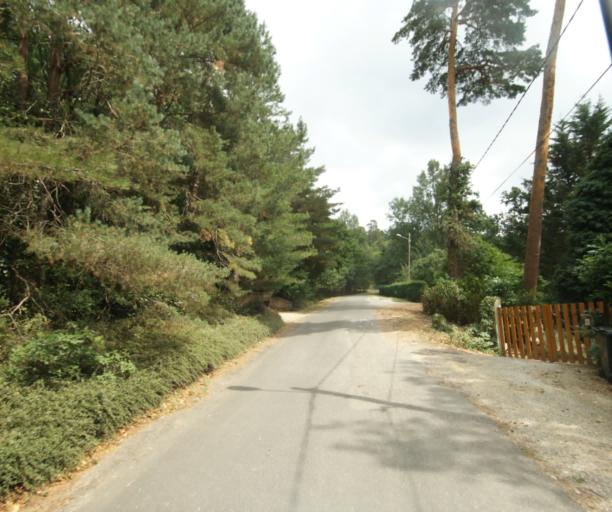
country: FR
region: Midi-Pyrenees
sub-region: Departement de la Haute-Garonne
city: Revel
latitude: 43.4311
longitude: 2.0327
